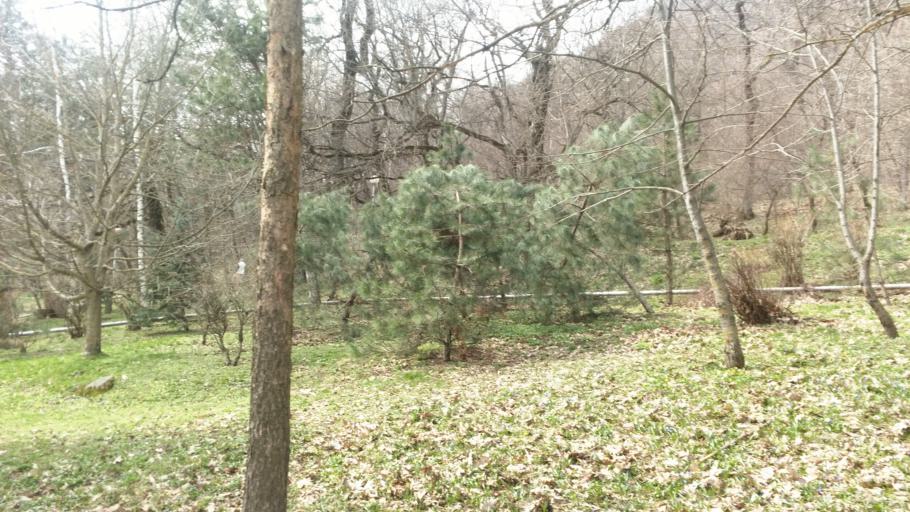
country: RU
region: Stavropol'skiy
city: Zheleznovodsk
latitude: 44.1370
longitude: 43.0342
